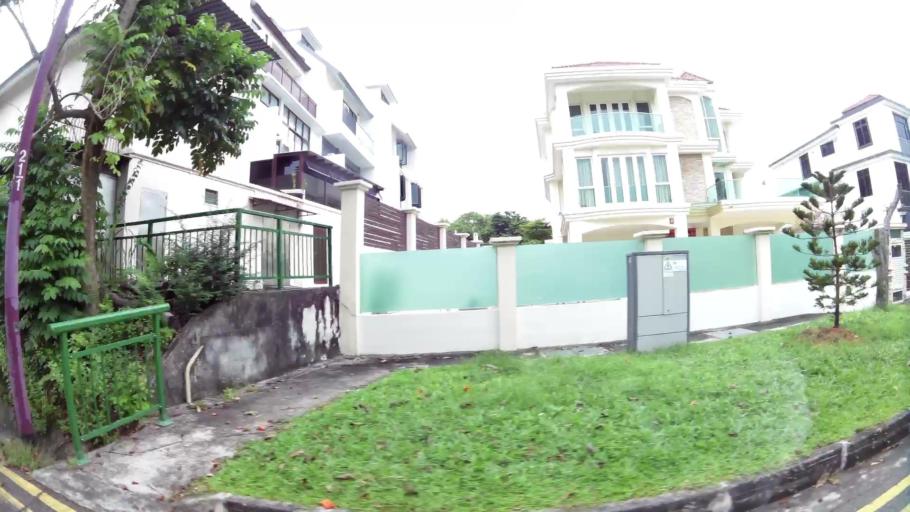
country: SG
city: Singapore
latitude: 1.3655
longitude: 103.8852
